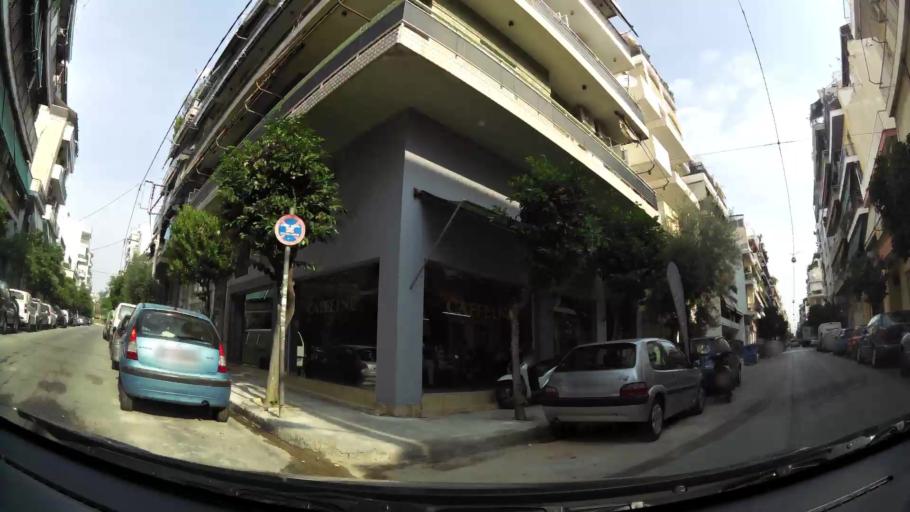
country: GR
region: Attica
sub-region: Nomarchia Athinas
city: Kallithea
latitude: 37.9552
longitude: 23.6944
